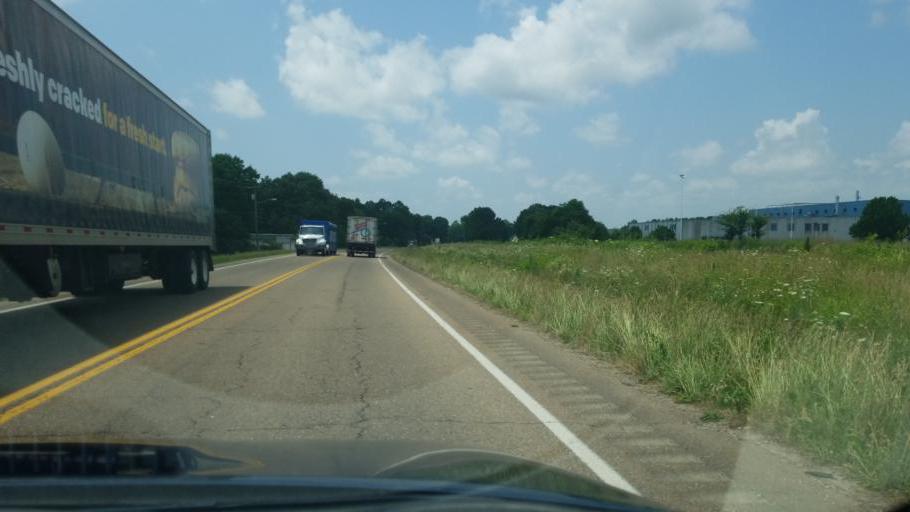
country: US
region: Tennessee
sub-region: Carroll County
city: Huntingdon
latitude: 36.0166
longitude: -88.3798
